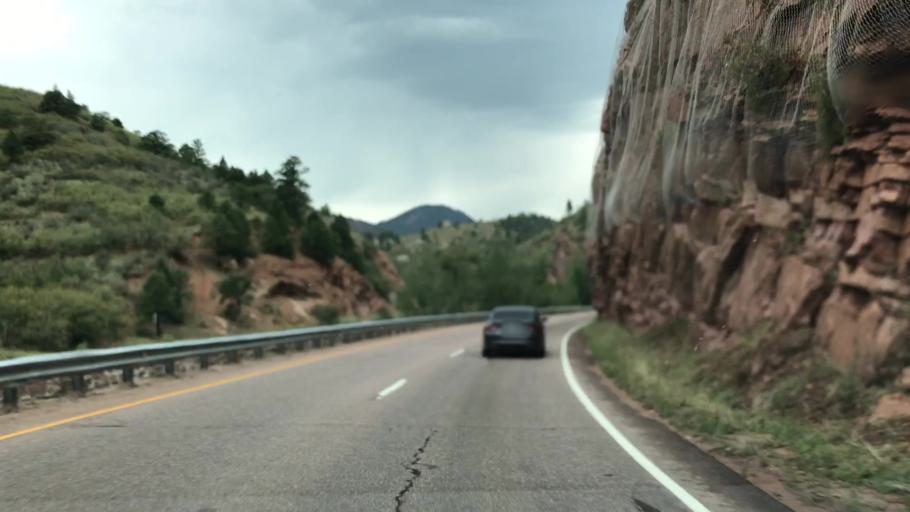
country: US
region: Colorado
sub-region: El Paso County
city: Manitou Springs
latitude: 38.8787
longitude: -104.9451
